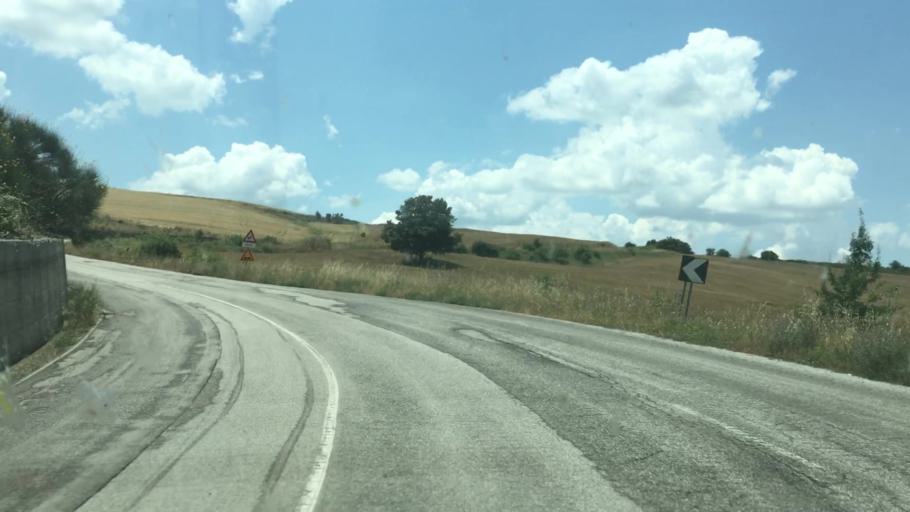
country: IT
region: Basilicate
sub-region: Provincia di Potenza
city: Tolve
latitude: 40.6860
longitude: 15.9793
